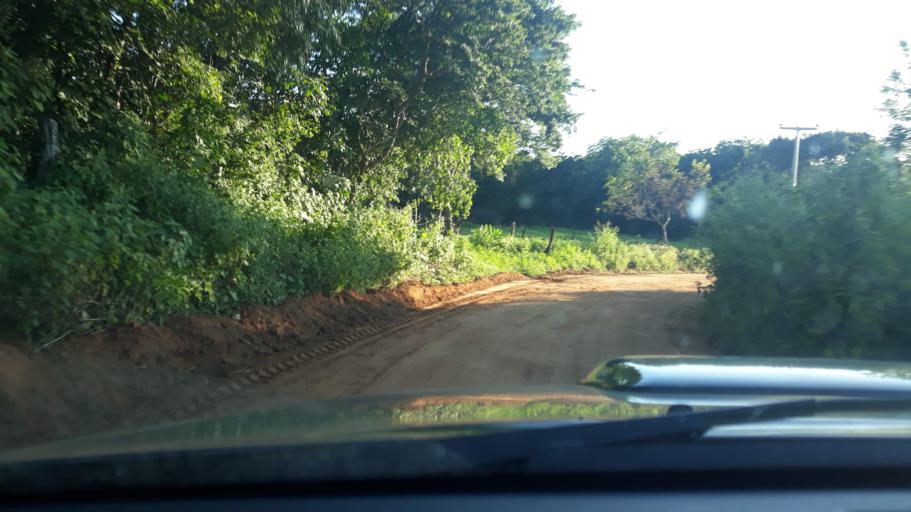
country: BR
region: Bahia
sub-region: Riacho De Santana
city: Riacho de Santana
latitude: -13.8453
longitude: -42.7415
